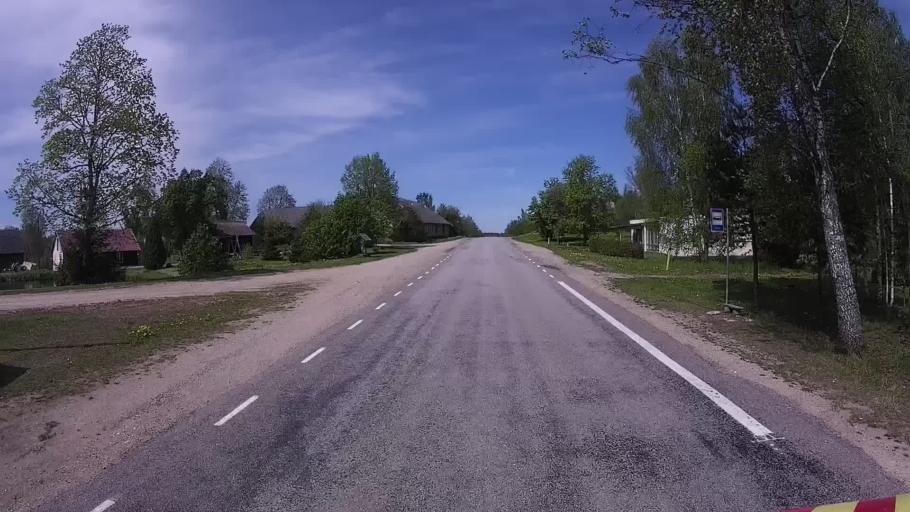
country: EE
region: Vorumaa
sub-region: Antsla vald
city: Vana-Antsla
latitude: 57.6283
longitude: 26.3435
